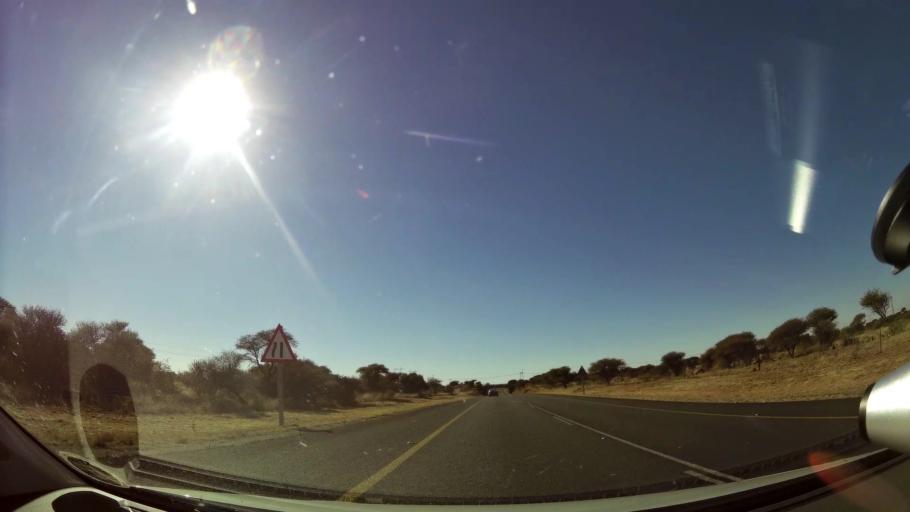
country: ZA
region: Northern Cape
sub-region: Frances Baard District Municipality
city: Warrenton
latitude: -28.0835
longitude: 24.8732
